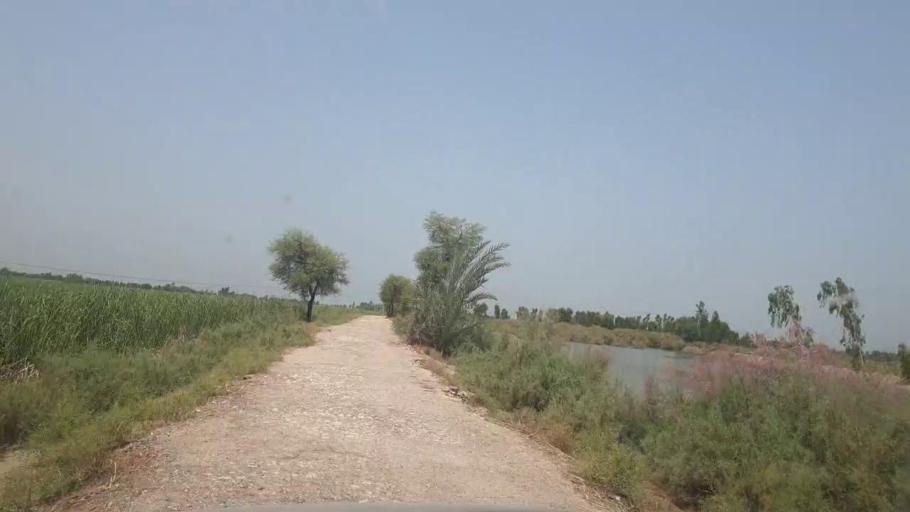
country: PK
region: Sindh
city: Lakhi
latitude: 27.8560
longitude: 68.6248
